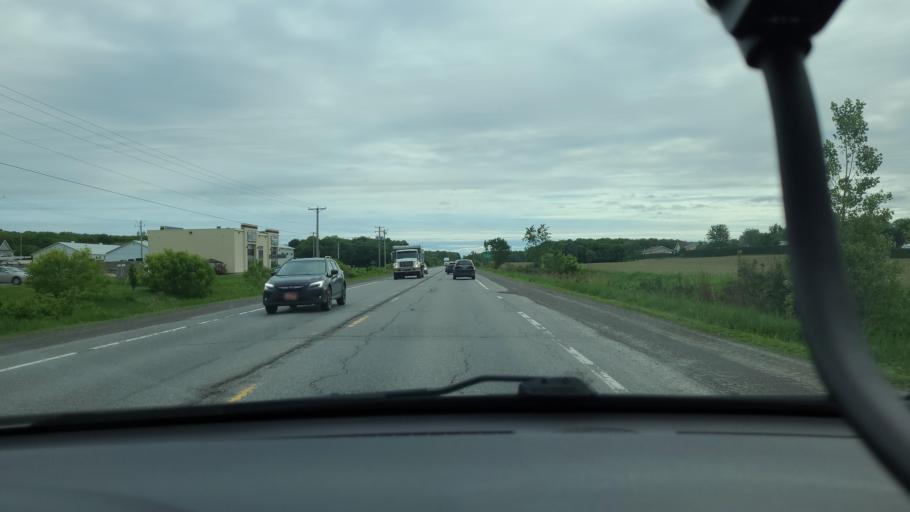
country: CA
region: Quebec
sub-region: Lanaudiere
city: Saint-Jacques
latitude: 45.9346
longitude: -73.6073
